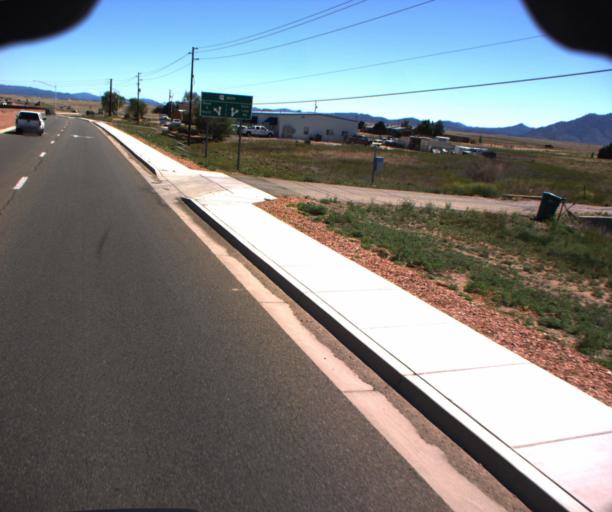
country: US
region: Arizona
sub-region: Yavapai County
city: Chino Valley
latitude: 34.7190
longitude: -112.4537
